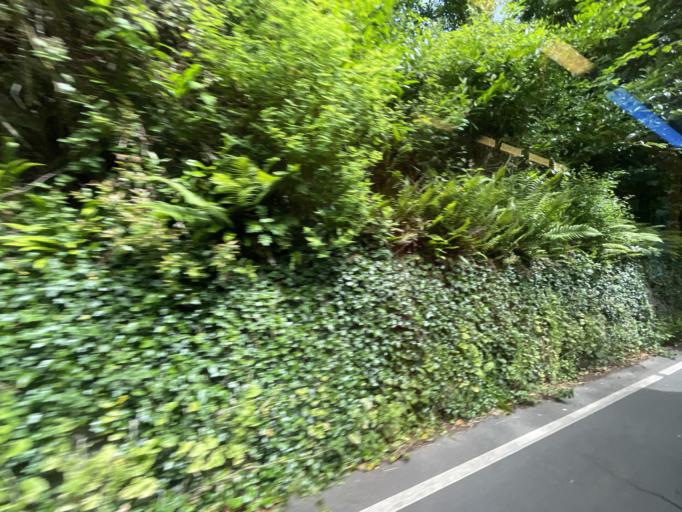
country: GB
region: Wales
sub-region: Anglesey
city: Beaumaris
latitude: 53.2654
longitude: -4.1042
